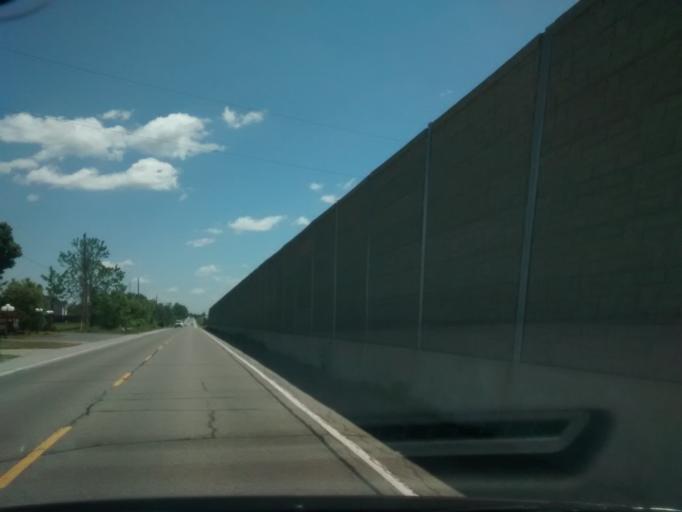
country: CA
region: Ontario
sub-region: Regional Municipality of Niagara
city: St. Catharines
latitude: 43.1798
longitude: -79.3452
